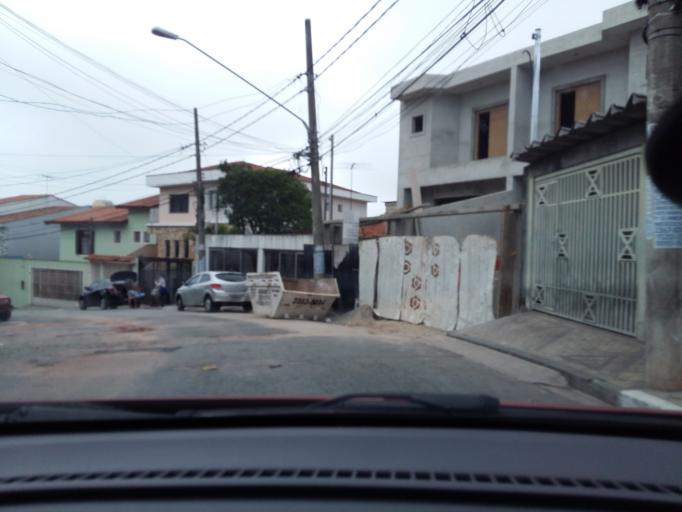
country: BR
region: Sao Paulo
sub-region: Sao Caetano Do Sul
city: Sao Caetano do Sul
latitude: -23.6385
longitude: -46.5983
